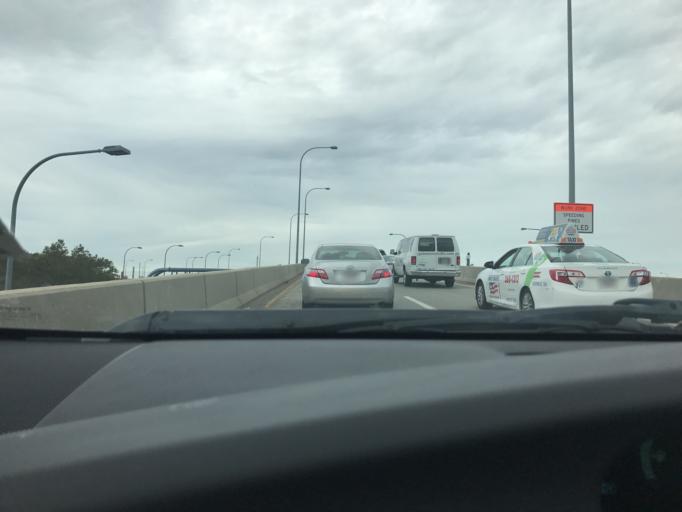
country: US
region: Massachusetts
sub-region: Suffolk County
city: Chelsea
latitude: 42.3729
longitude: -71.0289
